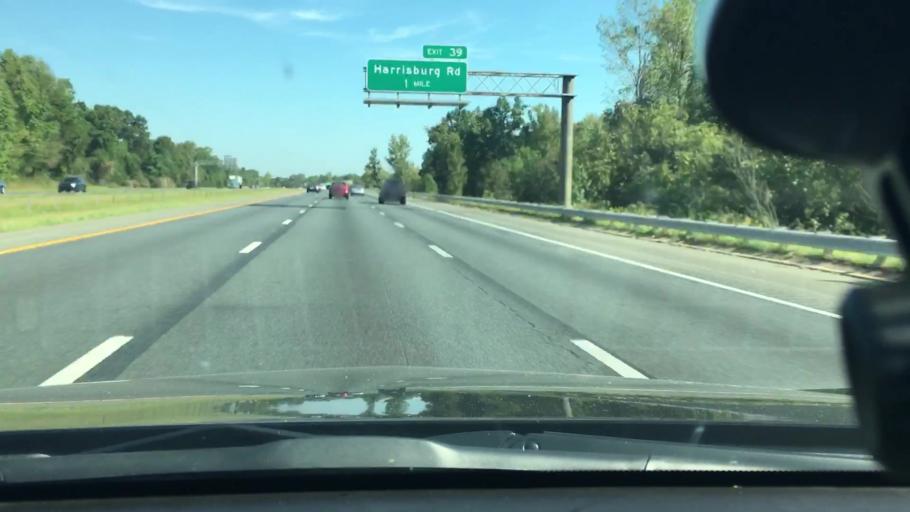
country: US
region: North Carolina
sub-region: Mecklenburg County
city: Mint Hill
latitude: 35.2354
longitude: -80.6528
